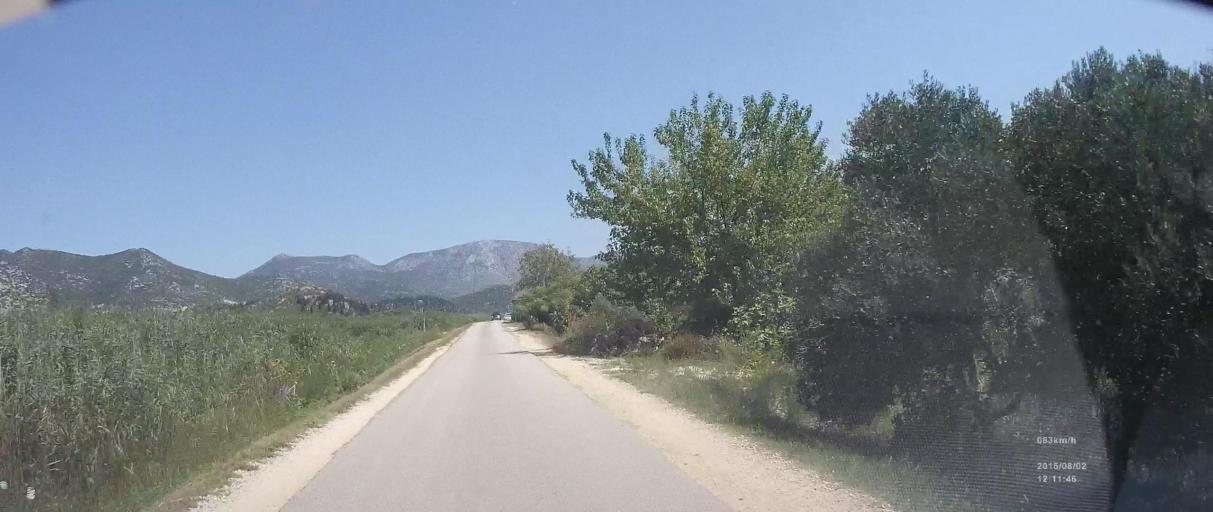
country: HR
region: Dubrovacko-Neretvanska
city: Komin
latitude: 43.0312
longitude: 17.4678
